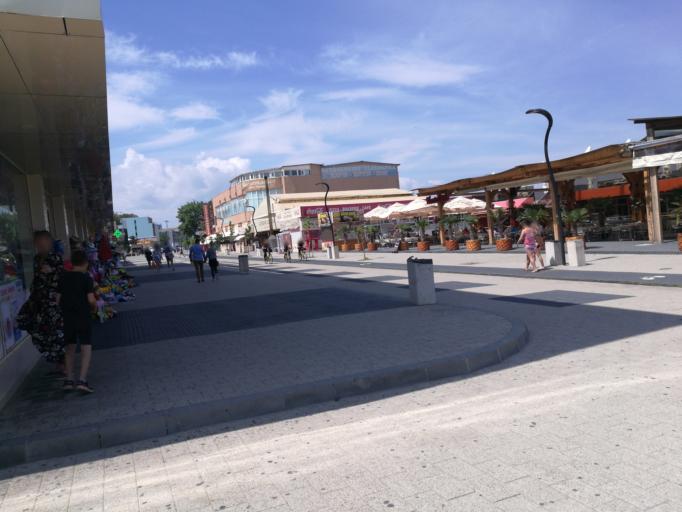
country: RO
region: Constanta
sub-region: Municipiul Constanta
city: Palazu Mare
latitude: 44.2218
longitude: 28.6339
